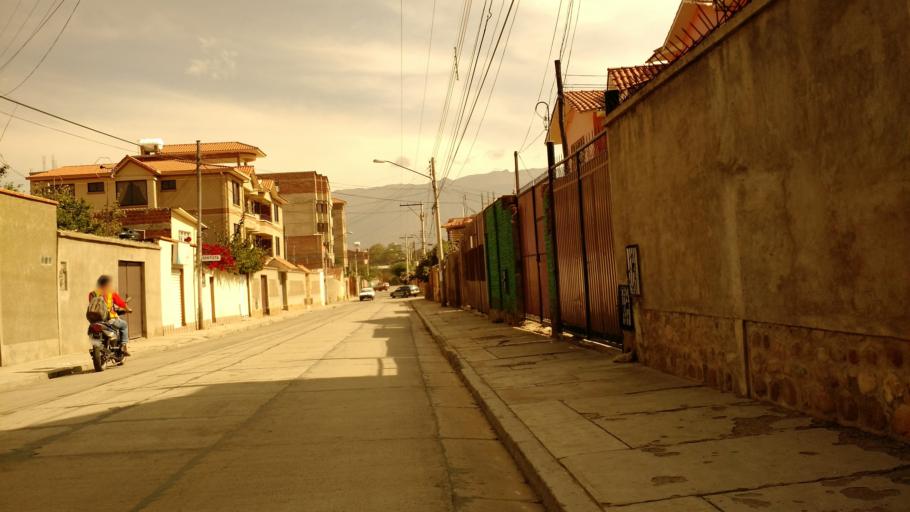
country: BO
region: Cochabamba
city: Cochabamba
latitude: -17.4244
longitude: -66.1597
